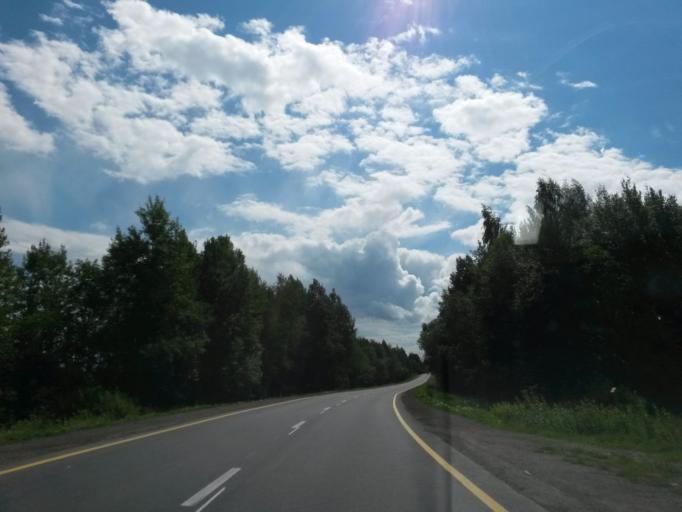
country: RU
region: Jaroslavl
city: Gavrilov-Yam
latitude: 57.2881
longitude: 39.9526
